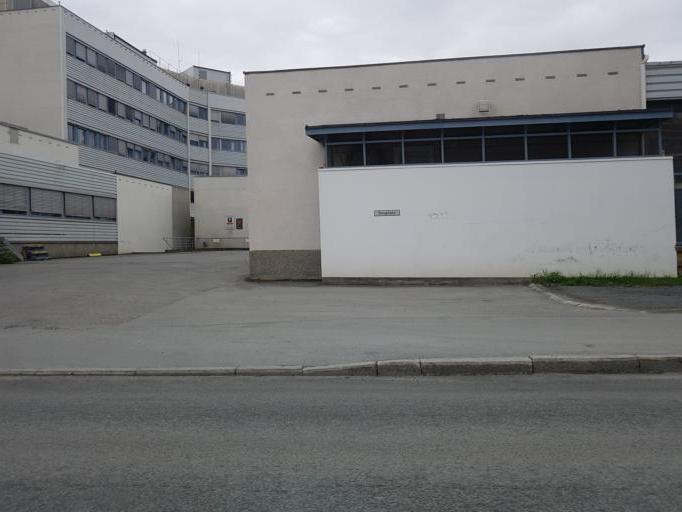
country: NO
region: Nord-Trondelag
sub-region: Levanger
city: Levanger
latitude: 63.7425
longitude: 11.2880
